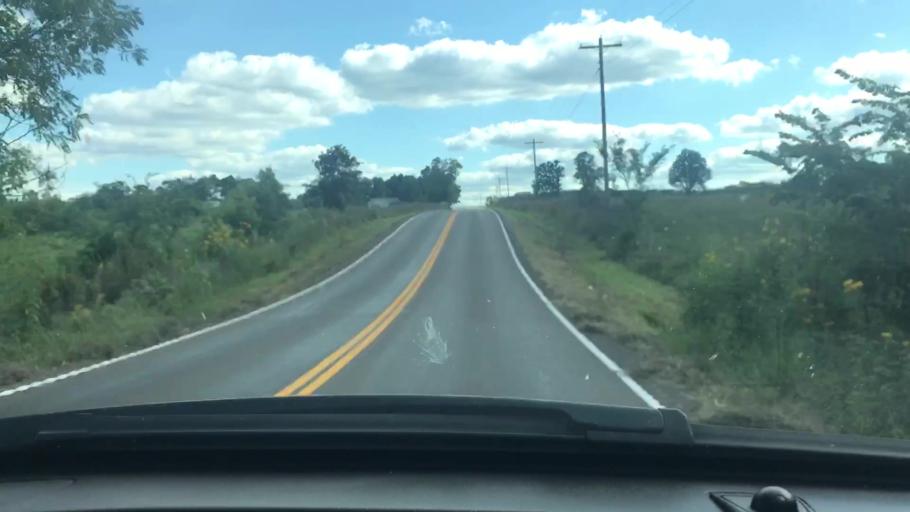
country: US
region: Missouri
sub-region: Wright County
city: Mountain Grove
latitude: 37.2388
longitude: -92.3005
